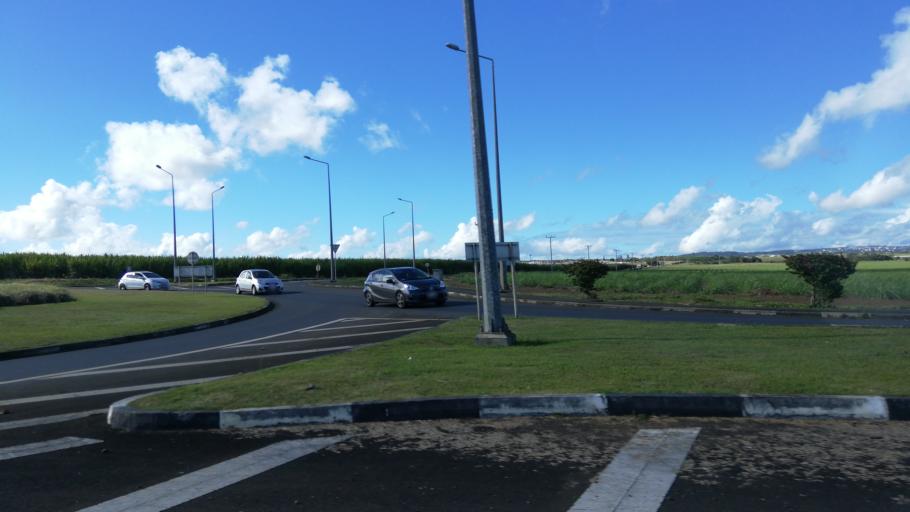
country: MU
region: Moka
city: Saint Pierre
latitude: -20.2307
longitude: 57.5272
